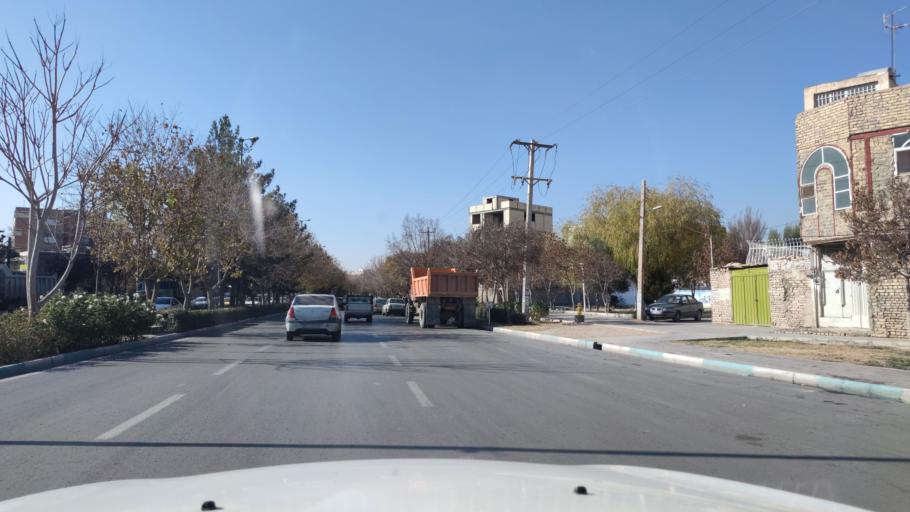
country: IR
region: Isfahan
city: Isfahan
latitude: 32.6804
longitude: 51.6518
